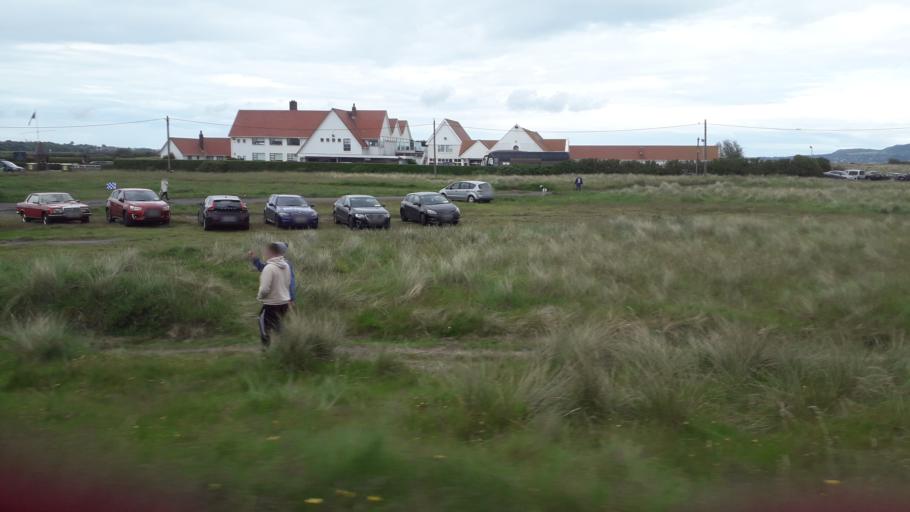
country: IE
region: Leinster
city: Dollymount
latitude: 53.3557
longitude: -6.1719
